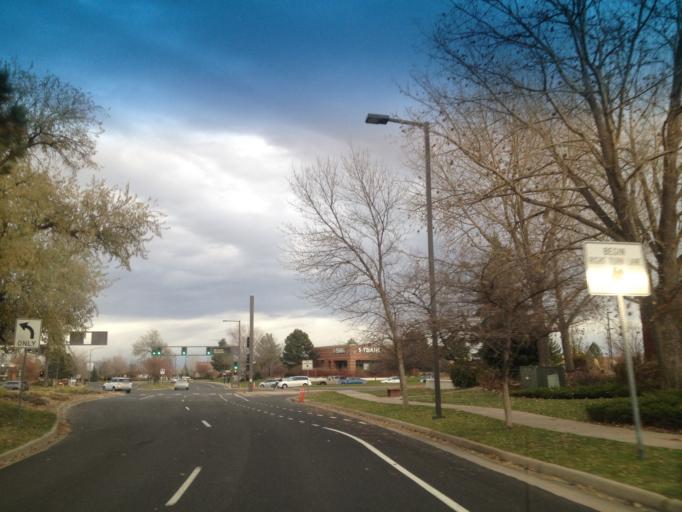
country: US
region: Colorado
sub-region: Boulder County
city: Superior
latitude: 39.9640
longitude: -105.1645
